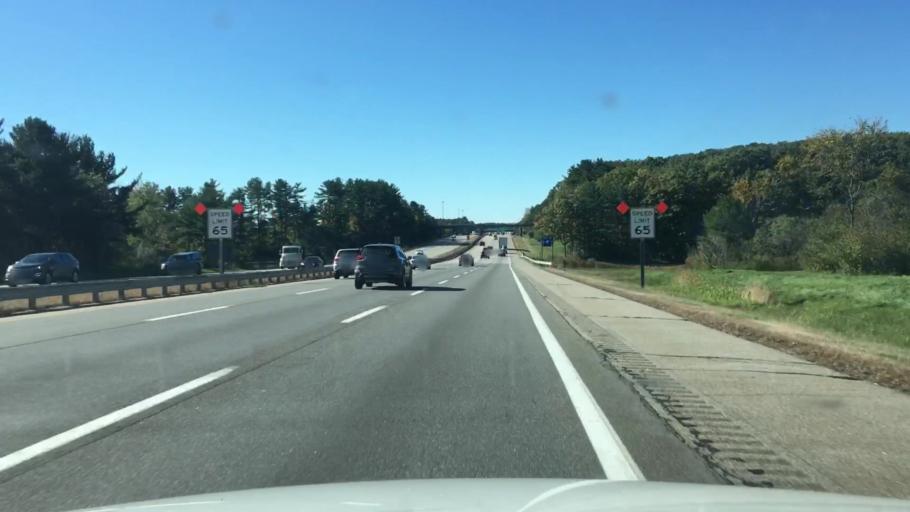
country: US
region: Maine
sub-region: York County
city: Kittery
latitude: 43.1163
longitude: -70.7328
